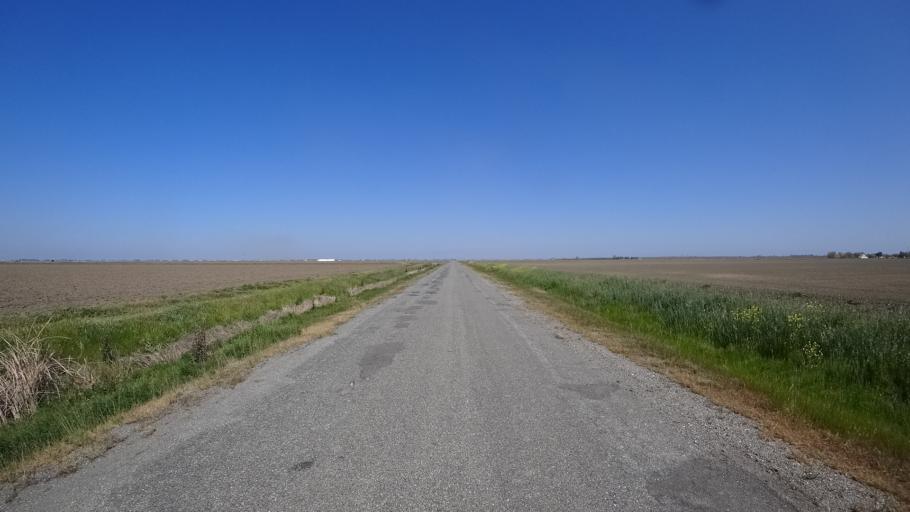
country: US
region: California
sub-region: Glenn County
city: Willows
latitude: 39.5166
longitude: -122.0372
